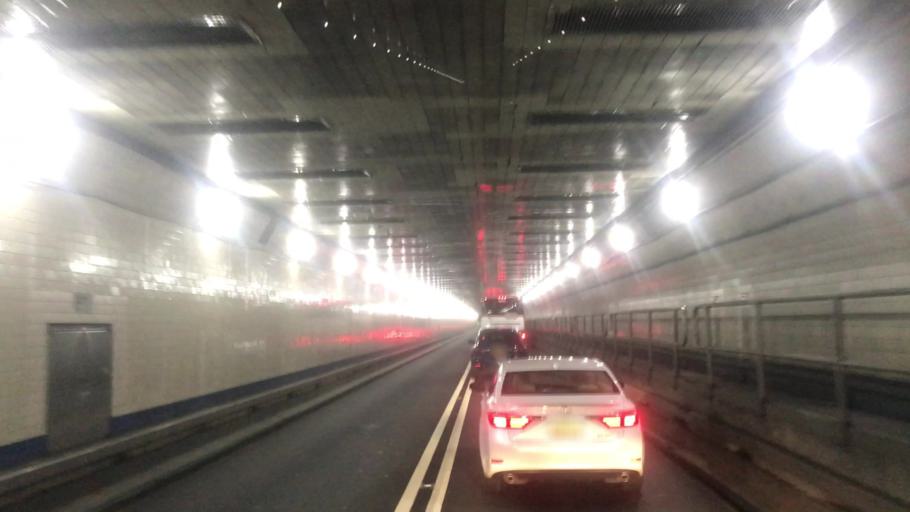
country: US
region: New Jersey
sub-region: Hudson County
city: Weehawken
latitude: 40.7637
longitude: -74.0203
